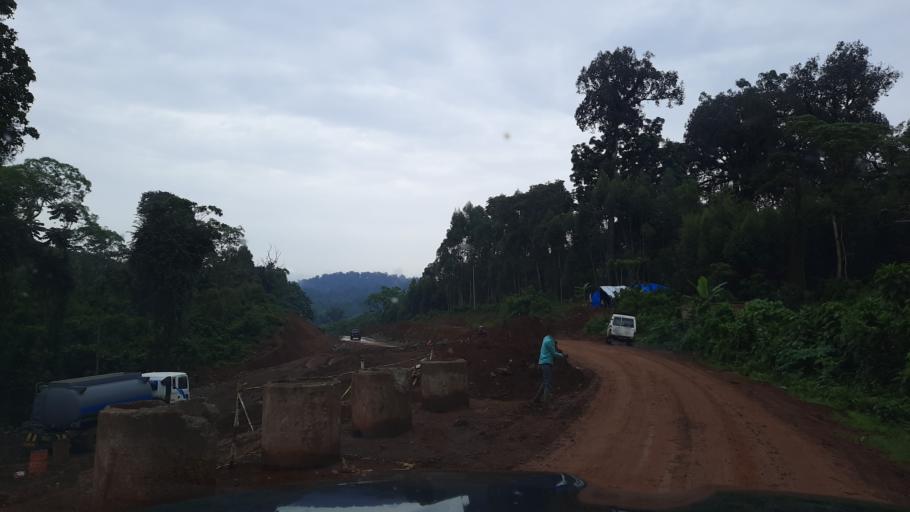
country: ET
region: Oromiya
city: Gore
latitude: 7.8646
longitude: 35.4798
